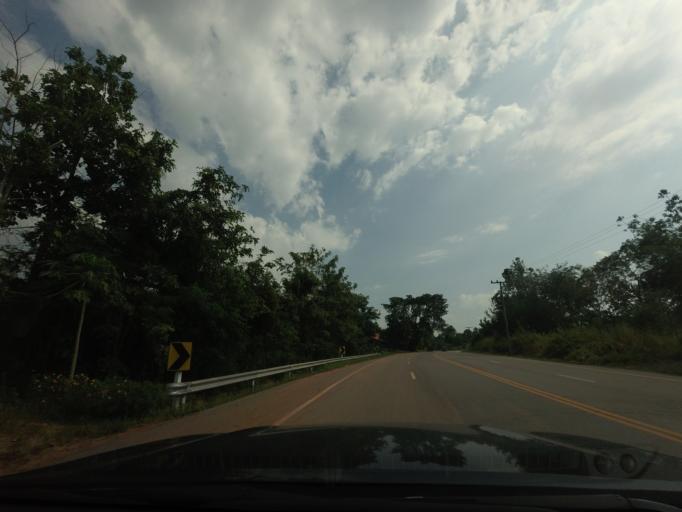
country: TH
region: Phitsanulok
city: Nakhon Thai
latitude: 17.0219
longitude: 100.9142
